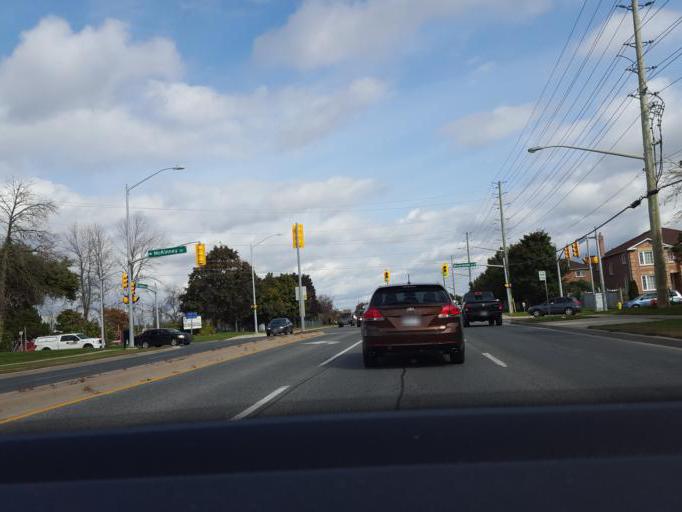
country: CA
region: Ontario
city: Ajax
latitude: 43.9163
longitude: -78.9529
